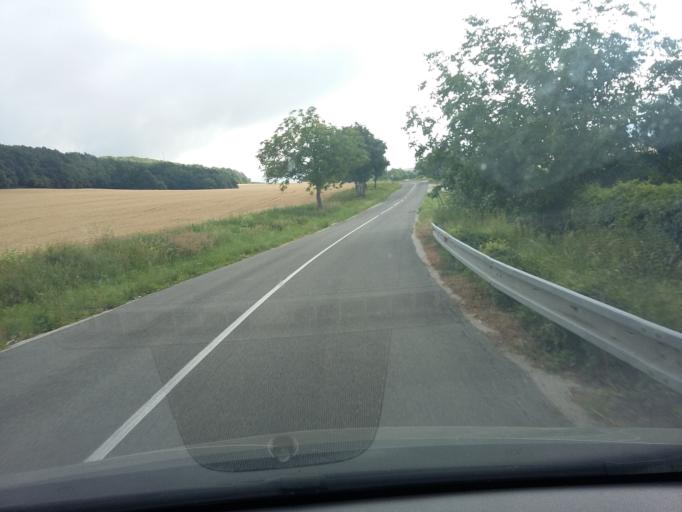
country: SK
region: Trnavsky
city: Smolenice
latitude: 48.5387
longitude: 17.3608
